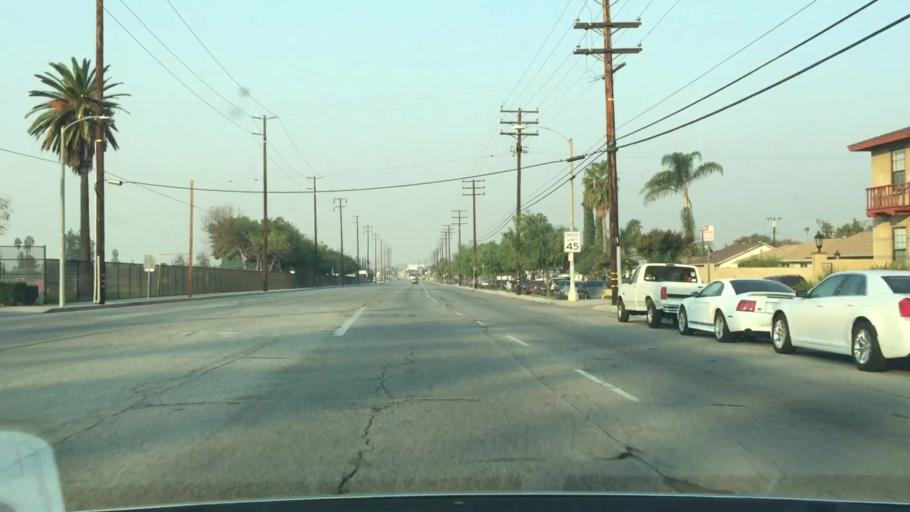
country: US
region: California
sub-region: Los Angeles County
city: Citrus
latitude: 34.1069
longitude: -117.9095
